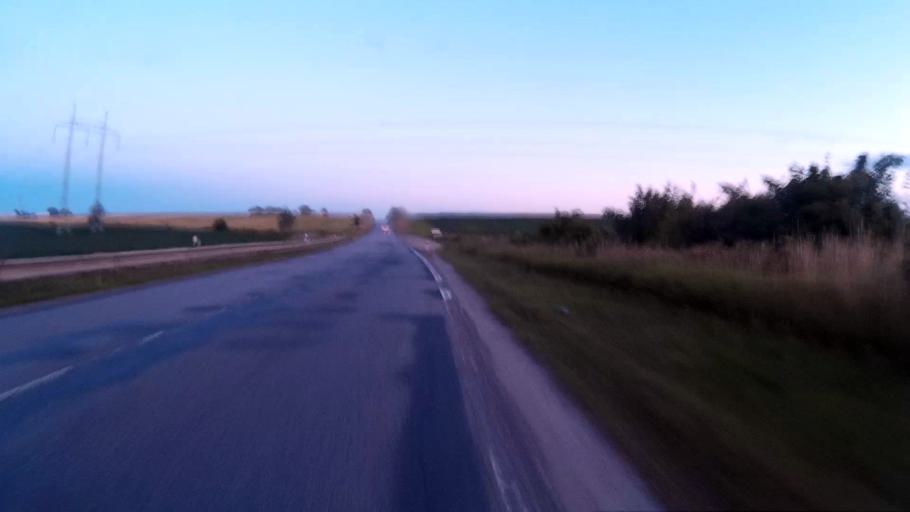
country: CZ
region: South Moravian
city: Troubsko
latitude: 49.1827
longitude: 16.5050
